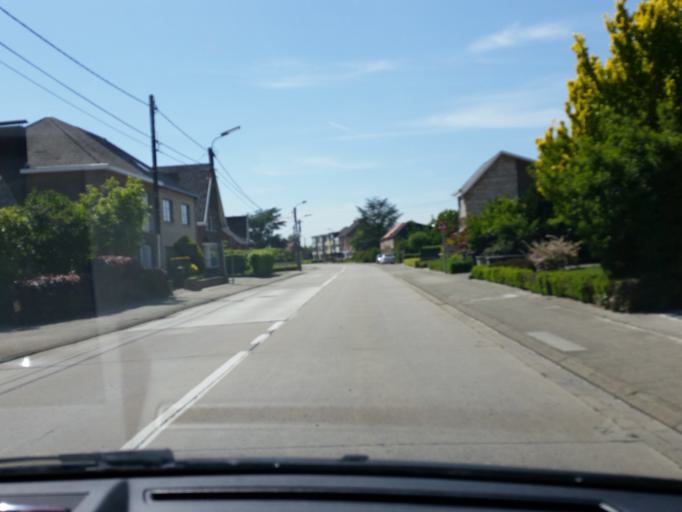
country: BE
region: Flanders
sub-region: Provincie Antwerpen
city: Sint-Katelijne-Waver
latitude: 51.0483
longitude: 4.5097
